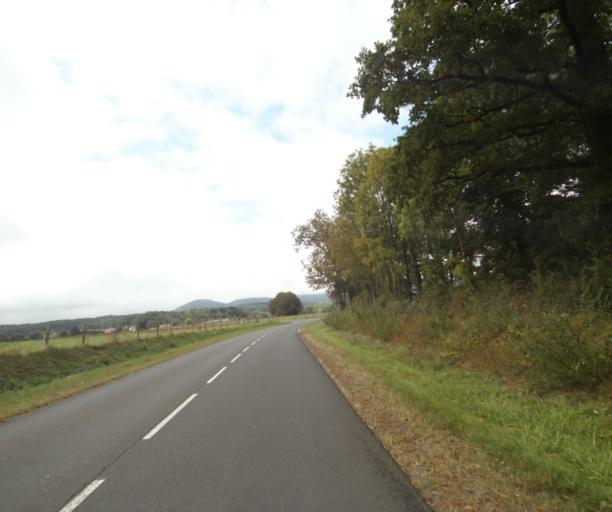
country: FR
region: Auvergne
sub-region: Departement du Puy-de-Dome
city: Saint-Genes-Champanelle
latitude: 45.7052
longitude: 3.0150
